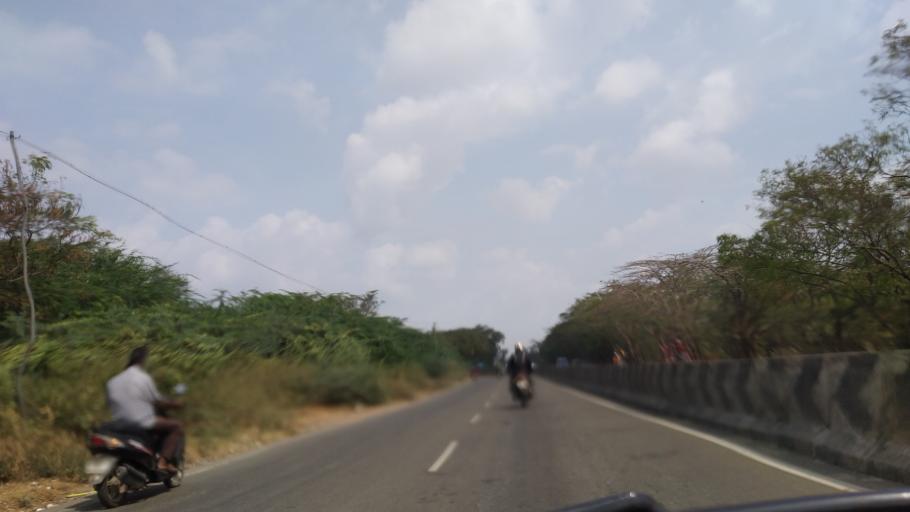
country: IN
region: Tamil Nadu
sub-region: Coimbatore
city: Madukkarai
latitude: 10.9192
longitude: 76.9487
